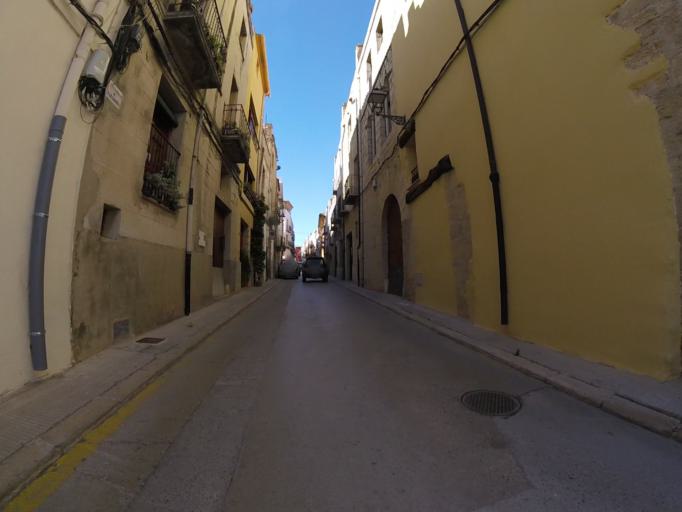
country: ES
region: Valencia
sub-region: Provincia de Castello
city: Chert/Xert
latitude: 40.4663
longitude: 0.1779
